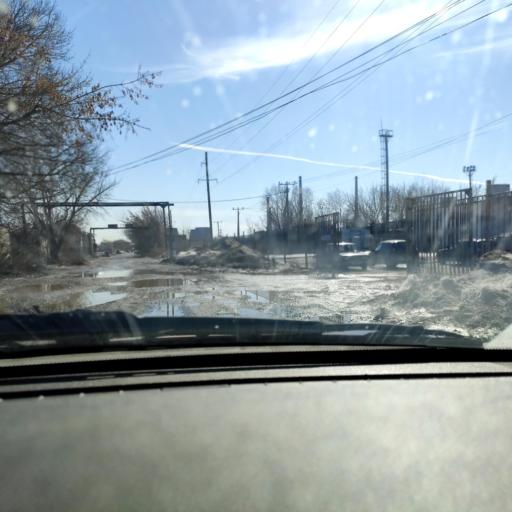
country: RU
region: Samara
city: Tol'yatti
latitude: 53.5892
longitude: 49.2582
